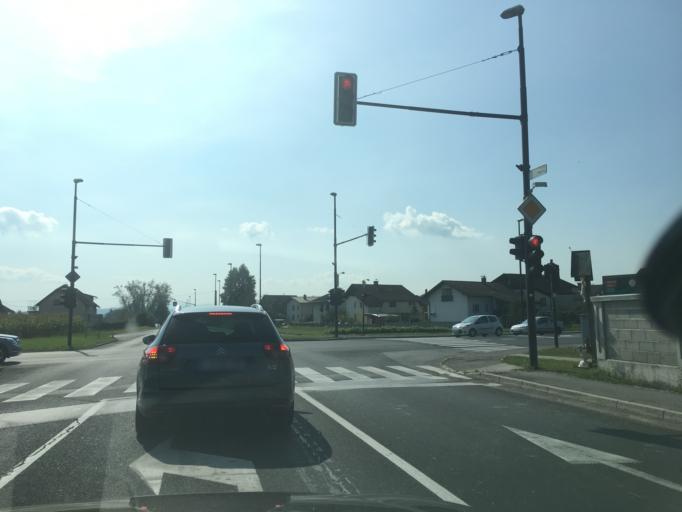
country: SI
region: Dol pri Ljubljani
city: Dol pri Ljubljani
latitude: 46.0916
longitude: 14.5832
